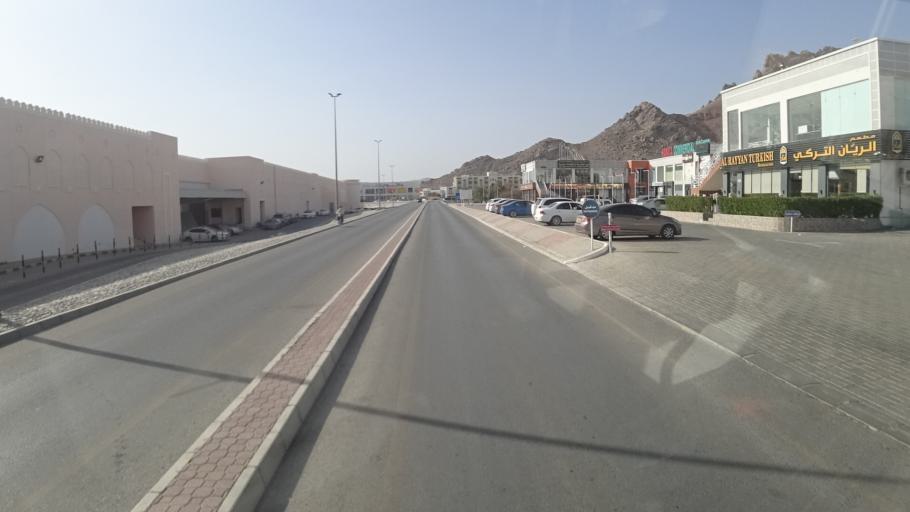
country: OM
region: Muhafazat ad Dakhiliyah
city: Nizwa
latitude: 22.8768
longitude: 57.5388
